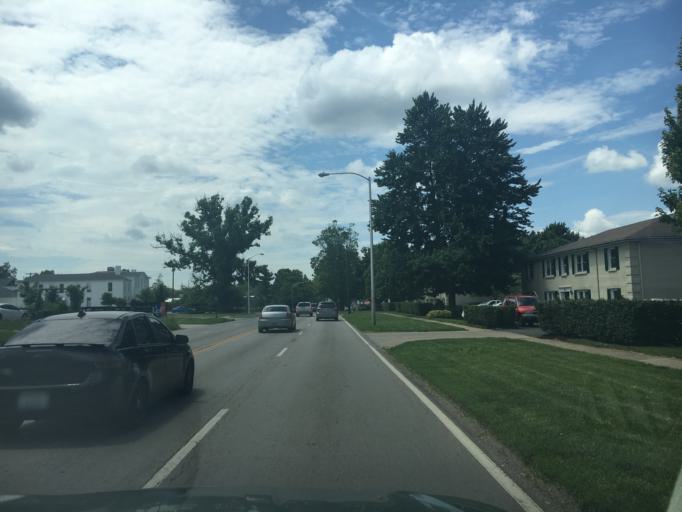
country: US
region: Kentucky
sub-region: Fayette County
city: Lexington-Fayette
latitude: 38.0620
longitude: -84.4812
